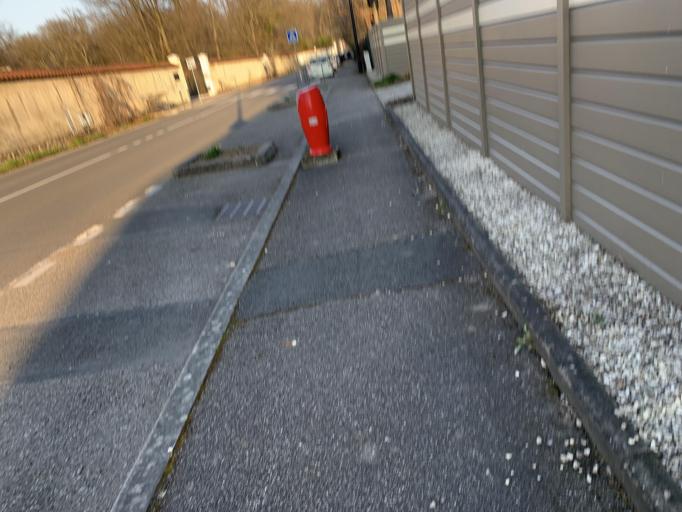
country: FR
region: Rhone-Alpes
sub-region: Departement du Rhone
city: Sainte-Consorce
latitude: 45.7846
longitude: 4.7211
